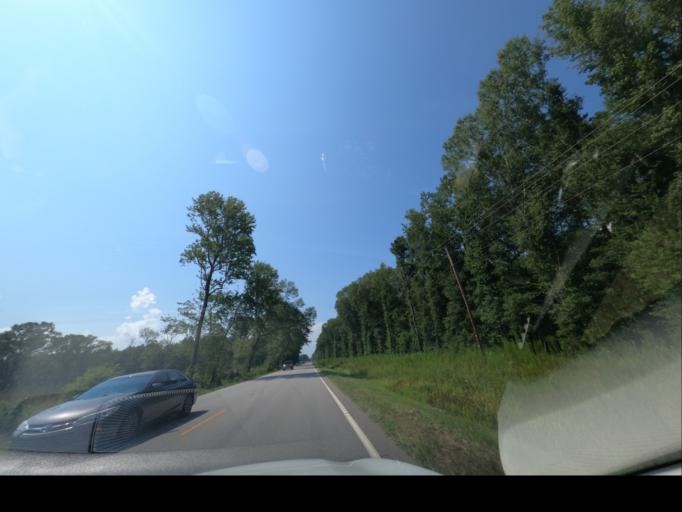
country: US
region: South Carolina
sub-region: Richland County
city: Hopkins
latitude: 33.8825
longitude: -80.9057
